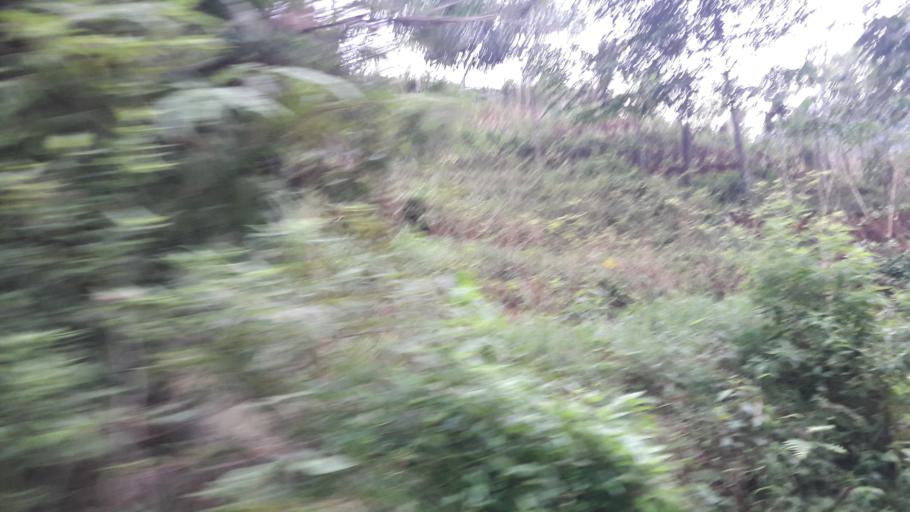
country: ID
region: West Java
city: Cipeundeuy
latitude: -6.6782
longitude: 106.5184
